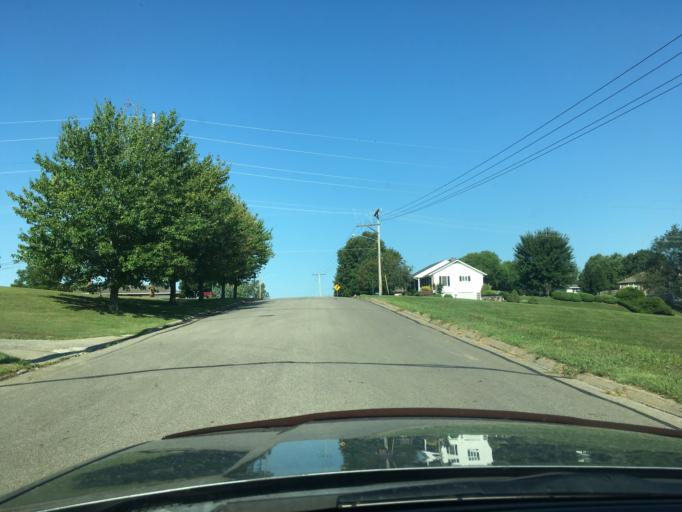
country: US
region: Kansas
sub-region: Atchison County
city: Atchison
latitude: 39.5782
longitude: -95.1235
